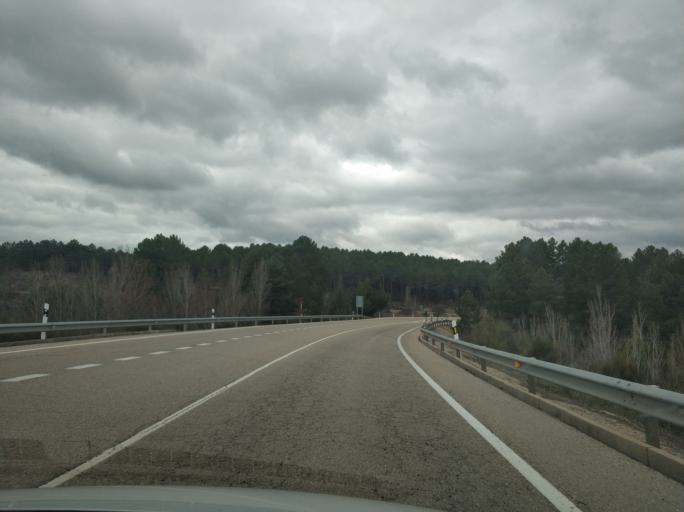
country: ES
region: Castille and Leon
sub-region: Provincia de Burgos
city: Pinilla de los Barruecos
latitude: 41.9049
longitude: -3.2756
